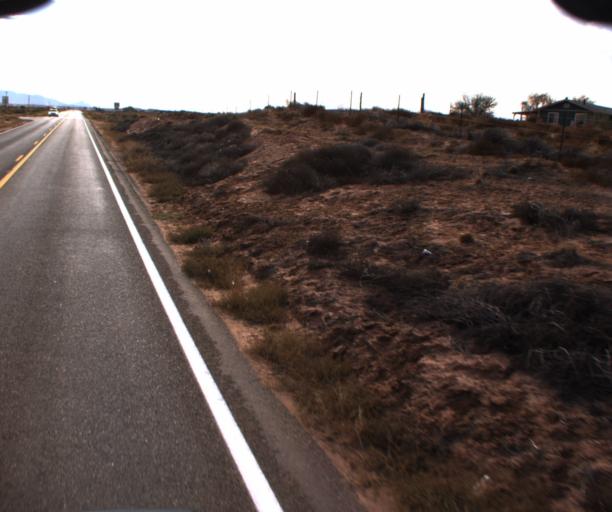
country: US
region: Arizona
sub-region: Apache County
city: Many Farms
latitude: 36.5107
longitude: -109.4752
